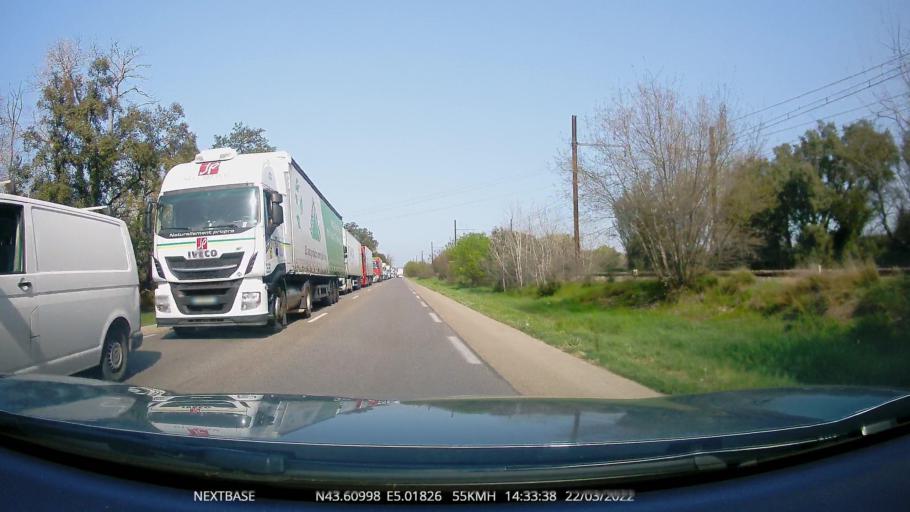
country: FR
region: Provence-Alpes-Cote d'Azur
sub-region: Departement des Bouches-du-Rhone
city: Miramas
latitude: 43.6100
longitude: 5.0183
